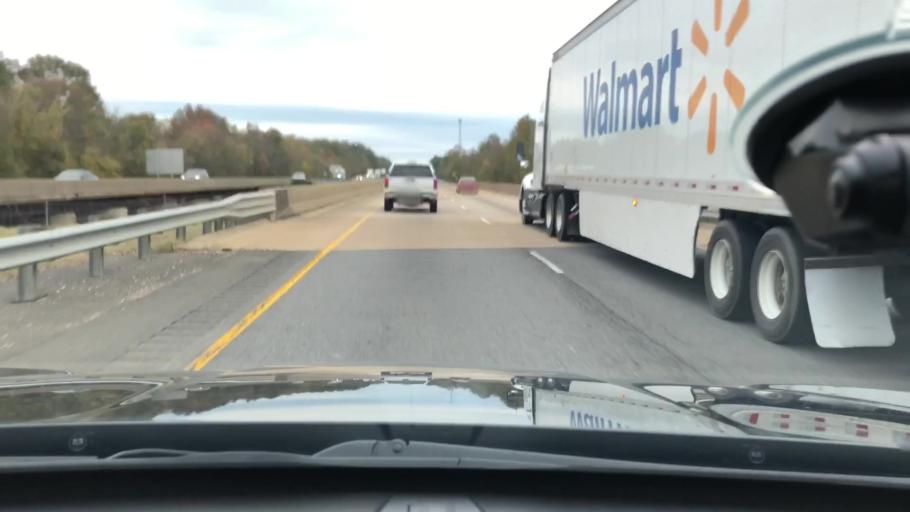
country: US
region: Arkansas
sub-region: Clark County
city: Gurdon
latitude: 34.0102
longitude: -93.1701
